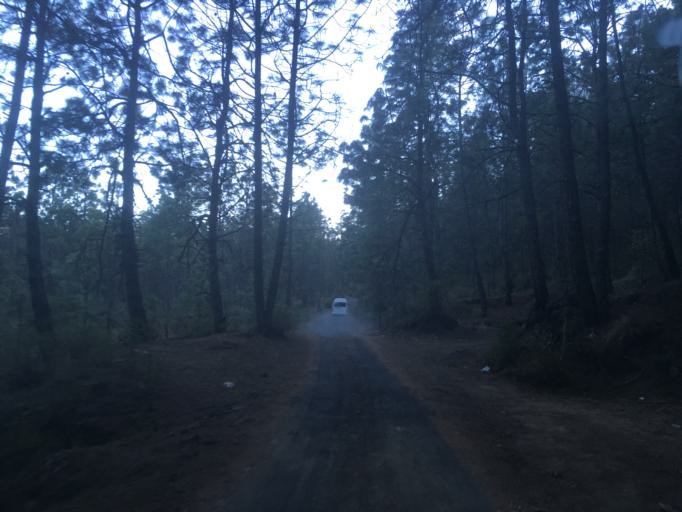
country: MX
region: Michoacan
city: Angahuan
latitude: 19.4693
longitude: -102.2401
